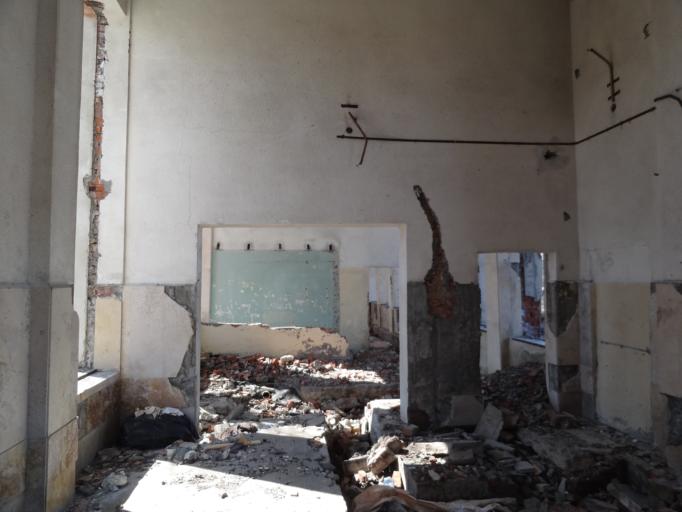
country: RU
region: Saratov
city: Shumeyka
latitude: 51.4099
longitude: 46.2446
